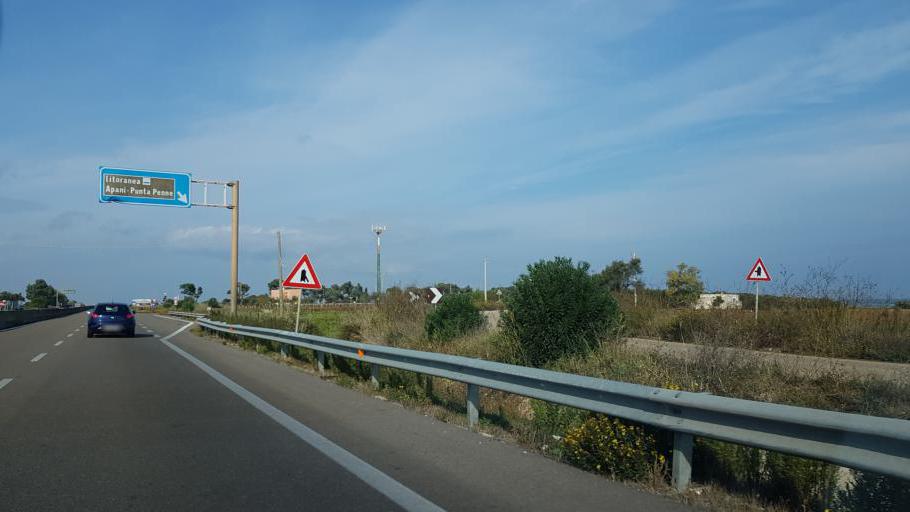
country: IT
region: Apulia
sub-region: Provincia di Brindisi
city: San Vito dei Normanni
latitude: 40.6908
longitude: 17.8220
